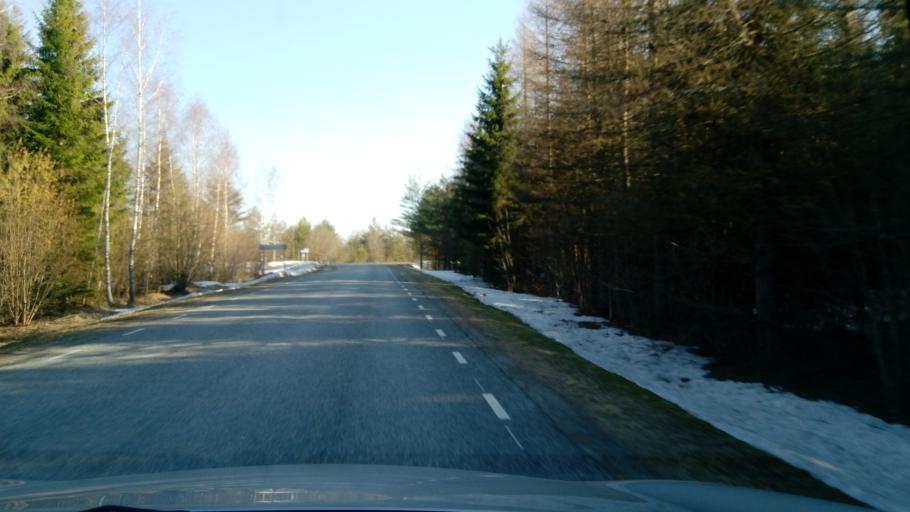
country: EE
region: Laeaene-Virumaa
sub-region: Kadrina vald
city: Kadrina
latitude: 59.2394
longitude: 26.1759
